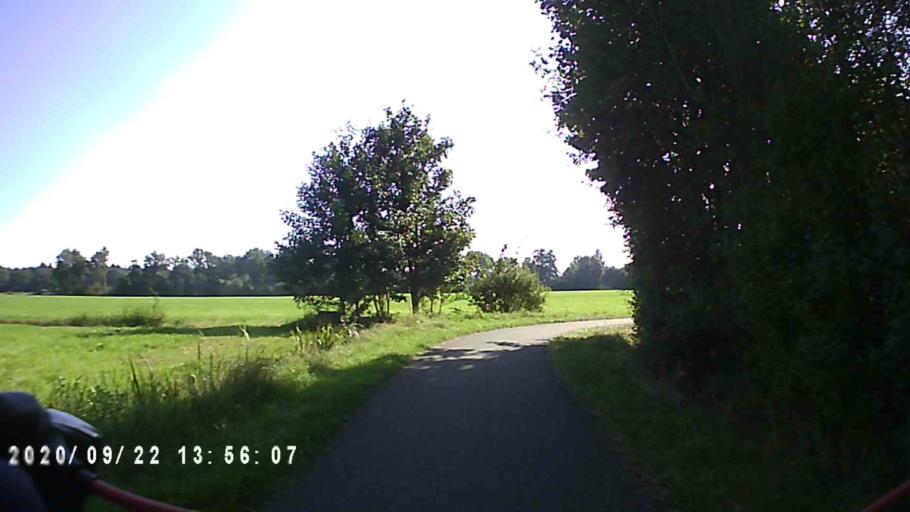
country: NL
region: Groningen
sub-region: Gemeente Leek
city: Leek
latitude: 53.1238
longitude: 6.4225
